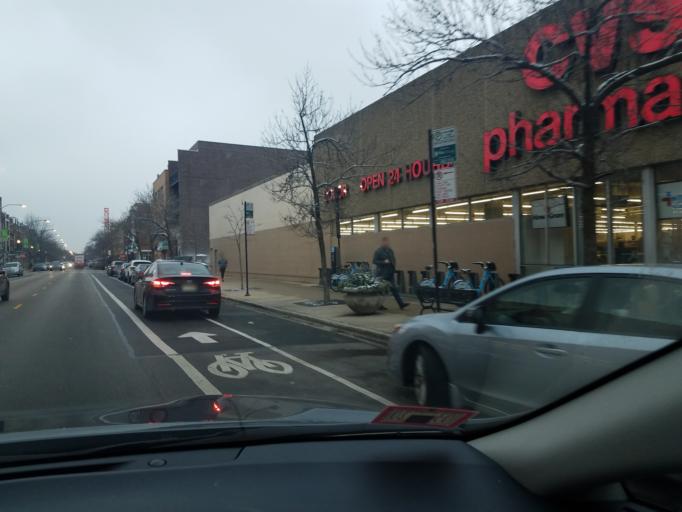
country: US
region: Illinois
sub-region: Cook County
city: Lincolnwood
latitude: 41.9480
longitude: -87.6641
